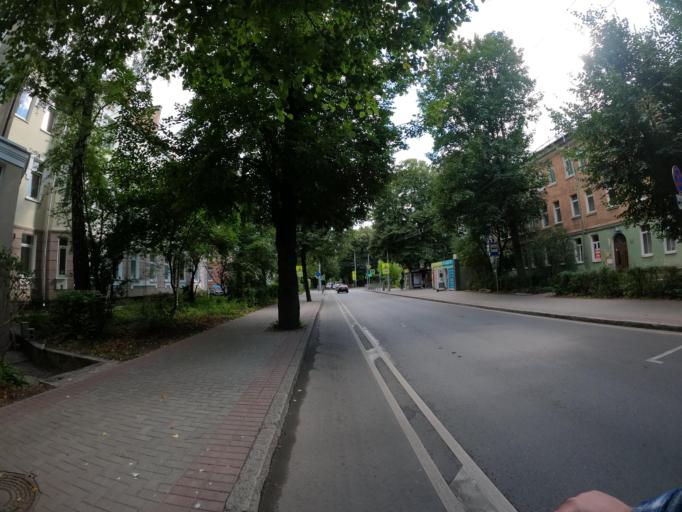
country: RU
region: Kaliningrad
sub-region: Gorod Kaliningrad
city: Kaliningrad
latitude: 54.7326
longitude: 20.4784
